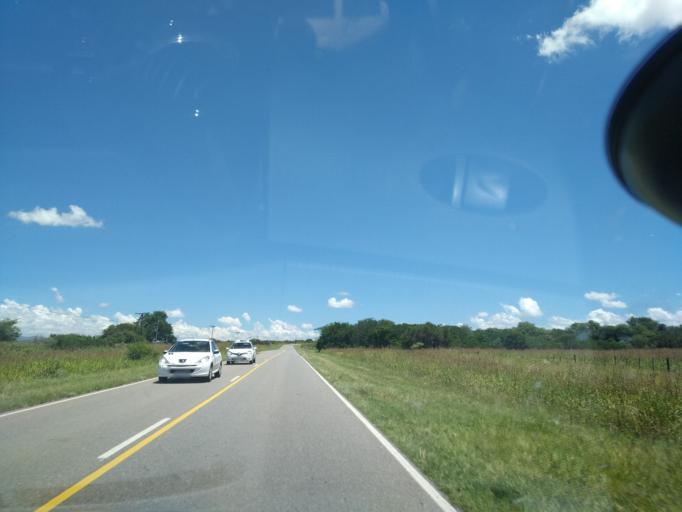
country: AR
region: Cordoba
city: Salsacate
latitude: -31.4032
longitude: -65.0967
